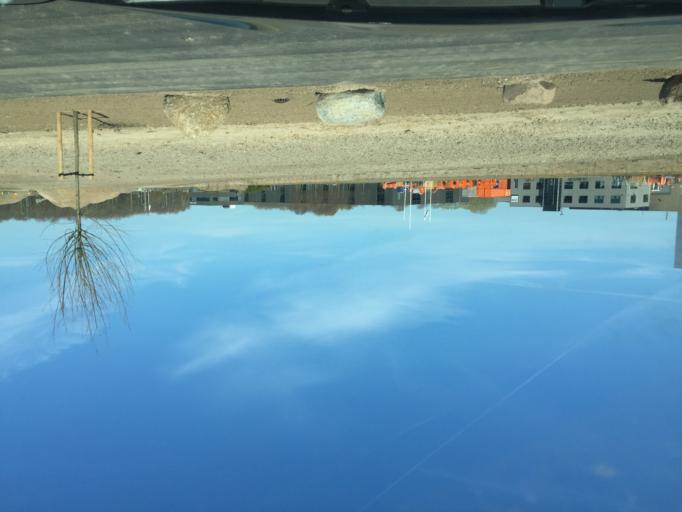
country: DK
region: South Denmark
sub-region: Odense Kommune
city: Hojby
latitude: 55.3544
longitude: 10.4189
